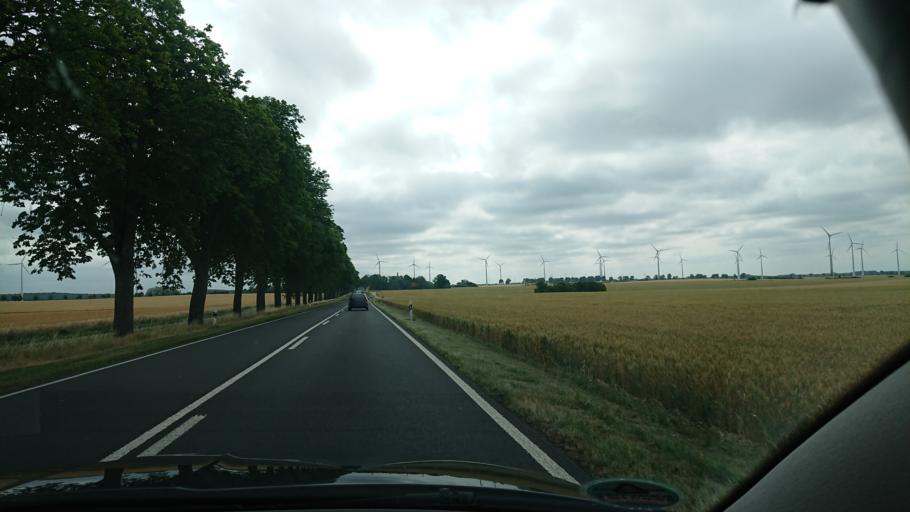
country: DE
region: Brandenburg
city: Plattenburg
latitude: 52.9989
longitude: 12.0755
